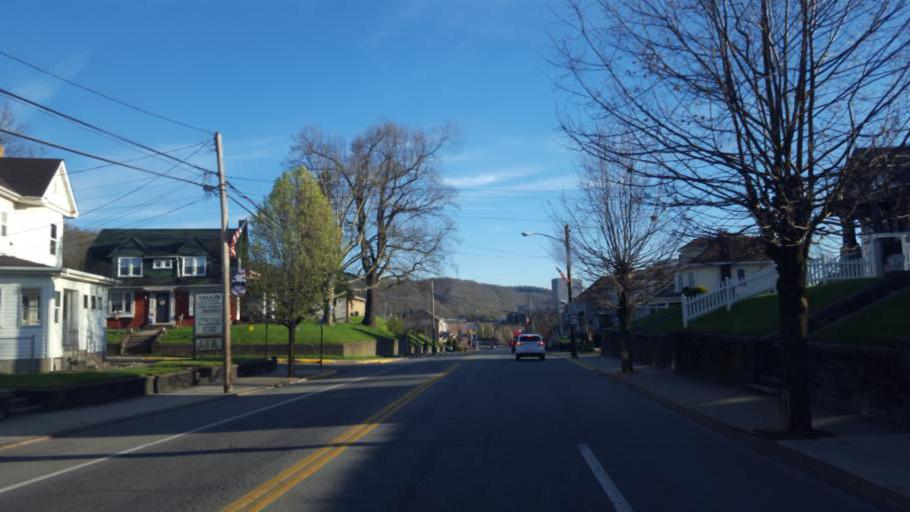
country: US
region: West Virginia
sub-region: Brooke County
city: Follansbee
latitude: 40.3324
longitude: -80.5963
